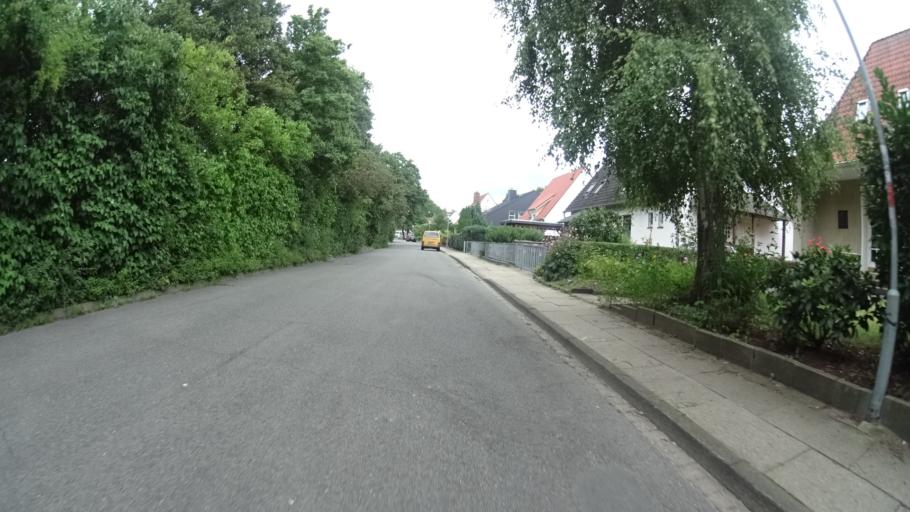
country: DE
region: Lower Saxony
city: Lueneburg
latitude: 53.2338
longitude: 10.3917
